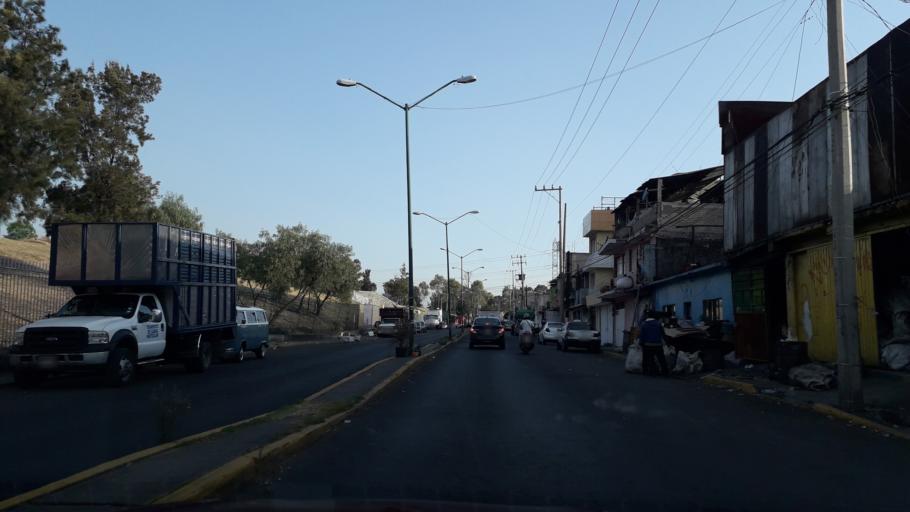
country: MX
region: Mexico City
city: Iztapalapa
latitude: 19.3673
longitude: -99.0477
